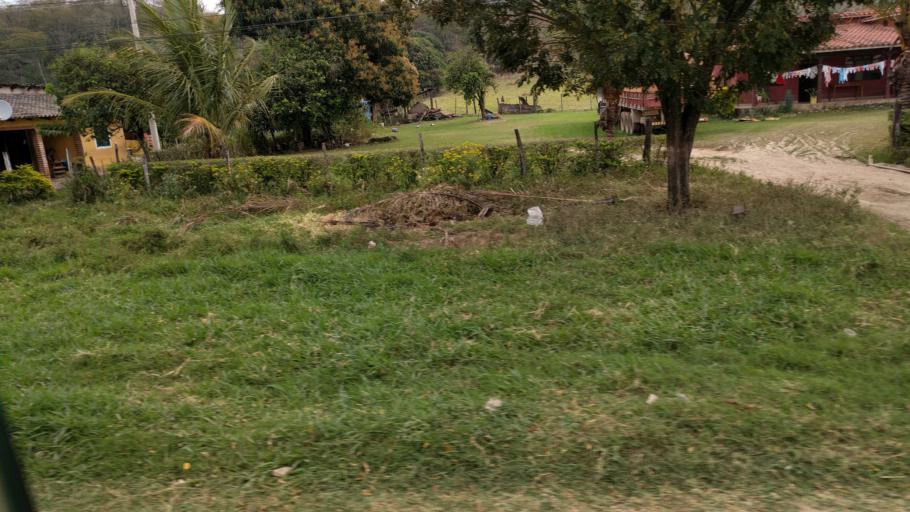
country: BO
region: Santa Cruz
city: Jorochito
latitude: -18.1223
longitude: -63.4637
